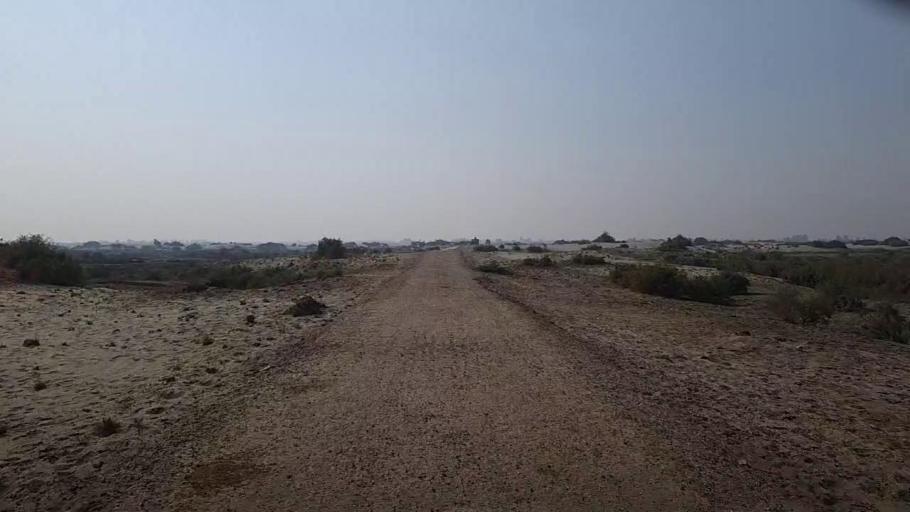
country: PK
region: Sindh
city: Bozdar
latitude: 27.2236
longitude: 68.5863
